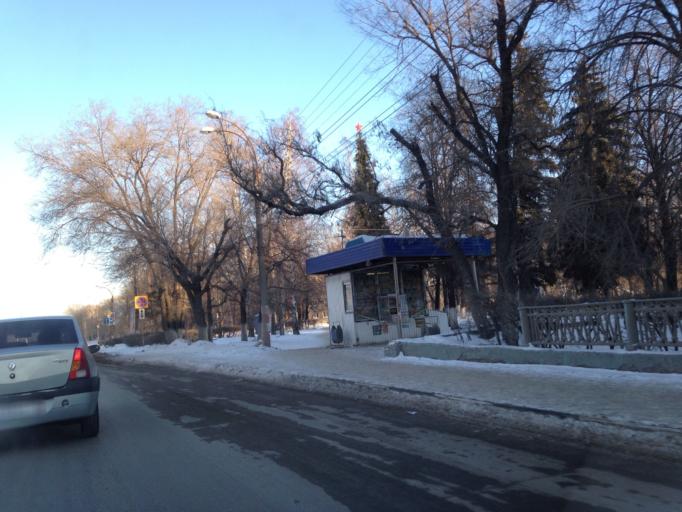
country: RU
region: Ulyanovsk
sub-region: Ulyanovskiy Rayon
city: Ulyanovsk
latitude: 54.2879
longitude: 48.3637
